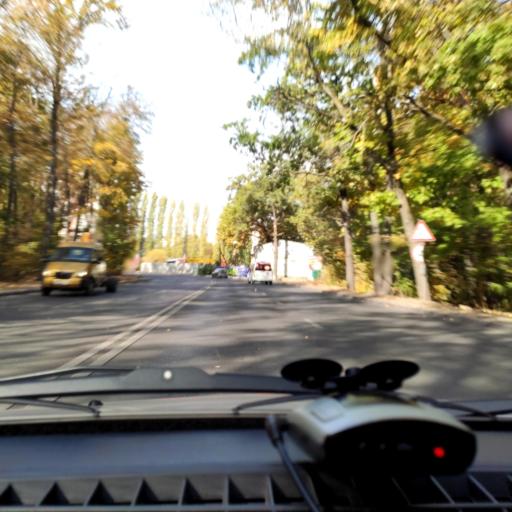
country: RU
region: Voronezj
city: Voronezh
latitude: 51.7261
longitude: 39.2143
